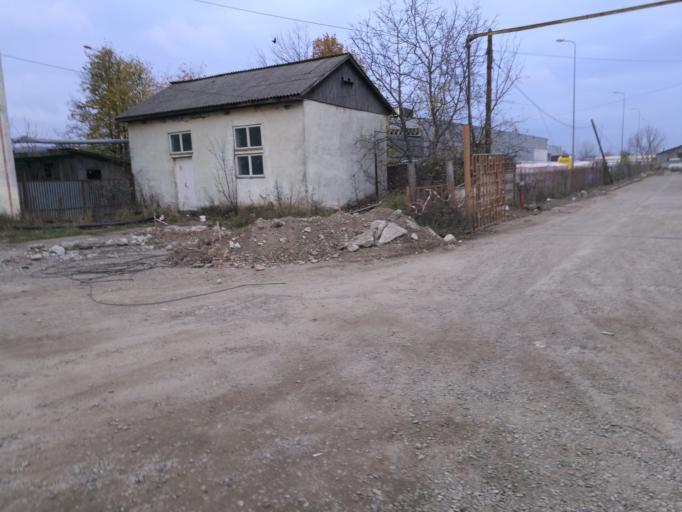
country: RO
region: Suceava
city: Suceava
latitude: 47.6659
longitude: 26.2702
